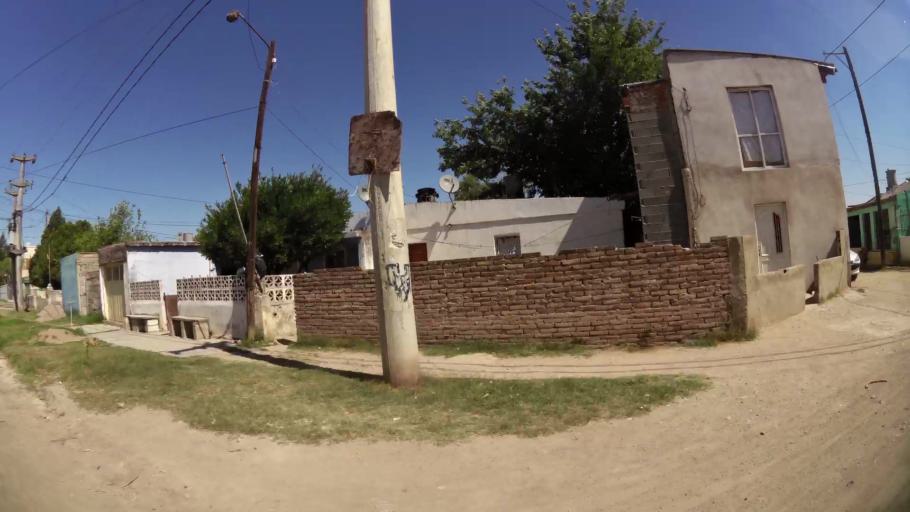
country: AR
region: Cordoba
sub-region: Departamento de Capital
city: Cordoba
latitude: -31.3657
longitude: -64.1420
